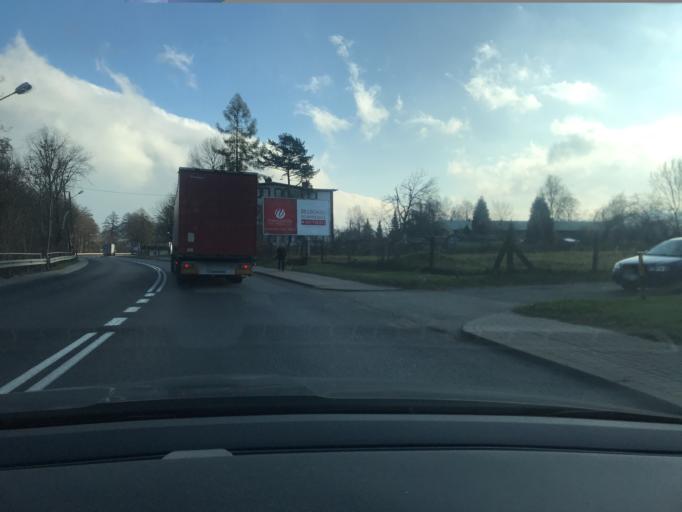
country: PL
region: Lower Silesian Voivodeship
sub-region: Powiat klodzki
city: Kudowa-Zdroj
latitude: 50.4305
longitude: 16.2458
